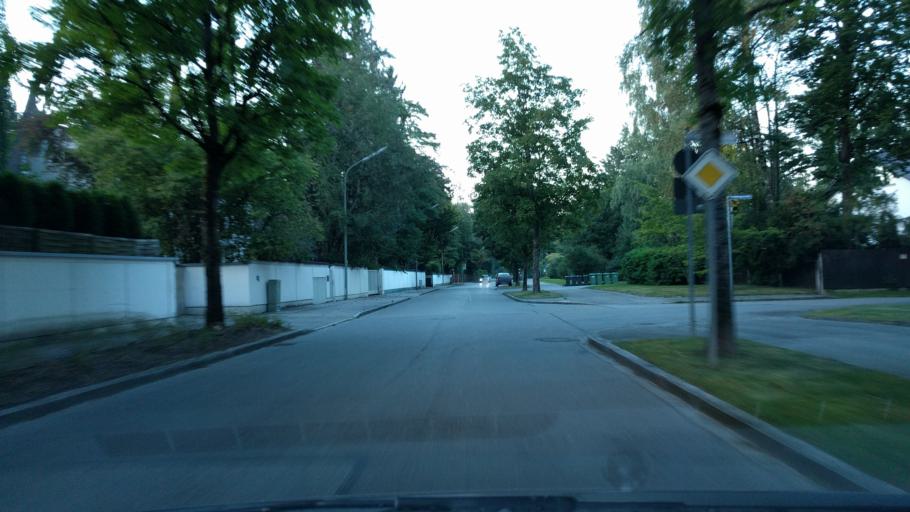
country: DE
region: Bavaria
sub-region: Upper Bavaria
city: Grunwald
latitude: 48.0456
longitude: 11.5391
